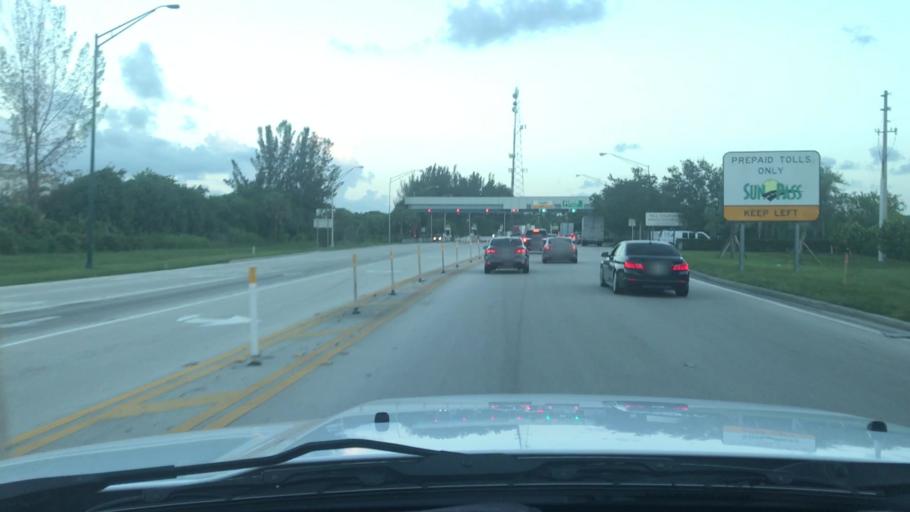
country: US
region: Florida
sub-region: Saint Lucie County
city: Fort Pierce South
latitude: 27.4120
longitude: -80.3990
